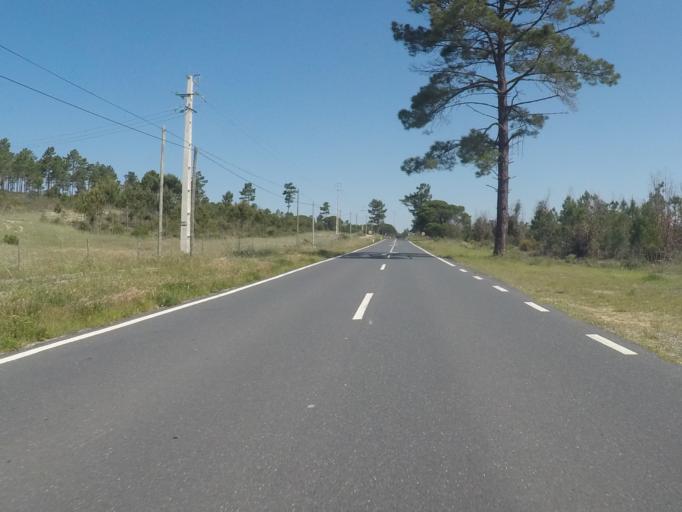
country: PT
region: Setubal
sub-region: Grandola
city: Grandola
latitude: 38.2340
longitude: -8.7361
